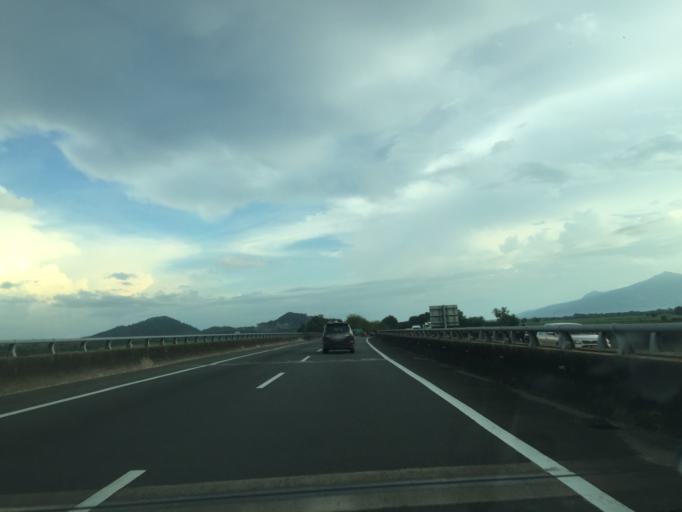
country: MY
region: Kedah
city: Gurun
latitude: 5.9729
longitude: 100.4438
